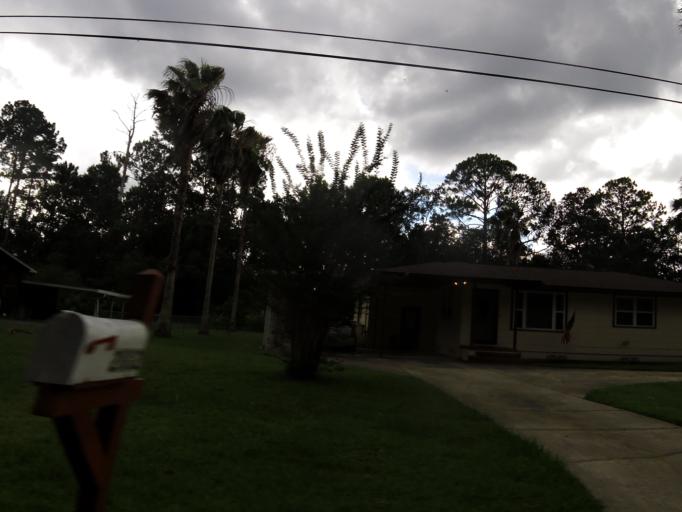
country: US
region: Florida
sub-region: Duval County
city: Jacksonville
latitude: 30.4220
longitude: -81.6942
